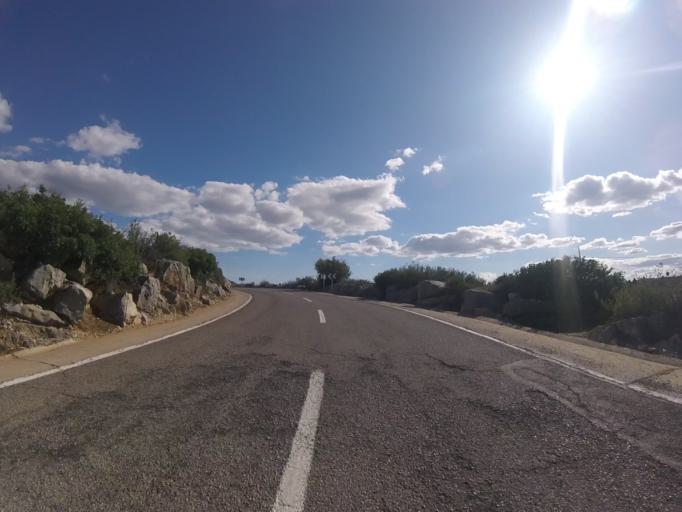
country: ES
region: Valencia
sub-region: Provincia de Castello
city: Alcala de Xivert
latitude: 40.2948
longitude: 0.1799
